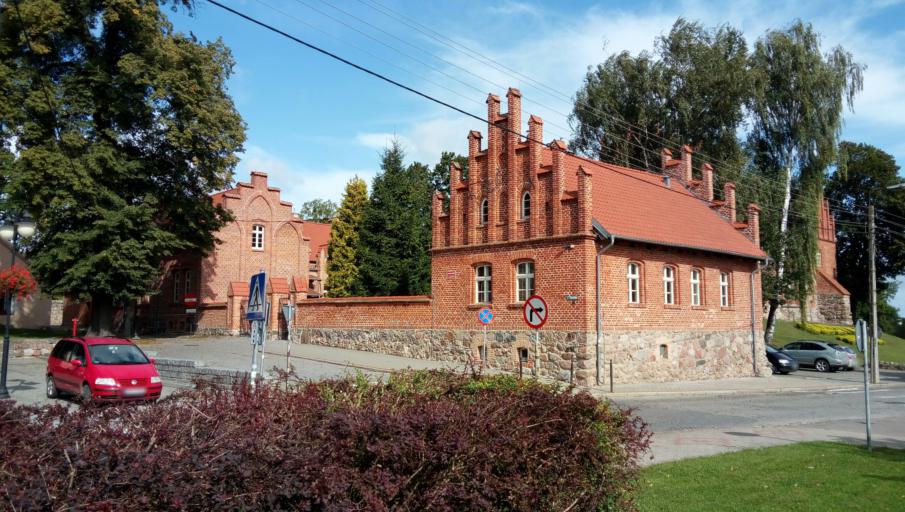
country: PL
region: Warmian-Masurian Voivodeship
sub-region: Powiat olsztynski
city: Olsztynek
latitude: 53.5830
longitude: 20.2839
